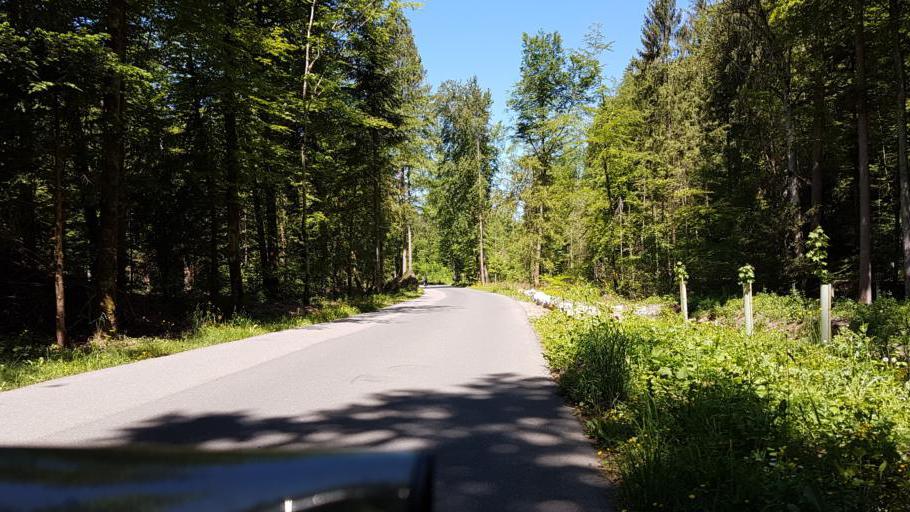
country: CH
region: Bern
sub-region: Thun District
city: Thierachern
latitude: 46.7299
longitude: 7.5908
